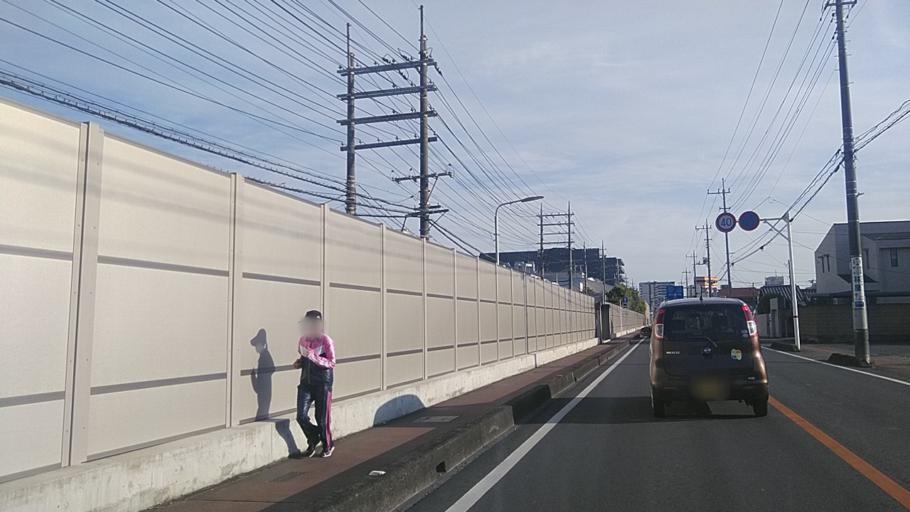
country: JP
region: Gunma
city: Ota
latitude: 36.2998
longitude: 139.3809
